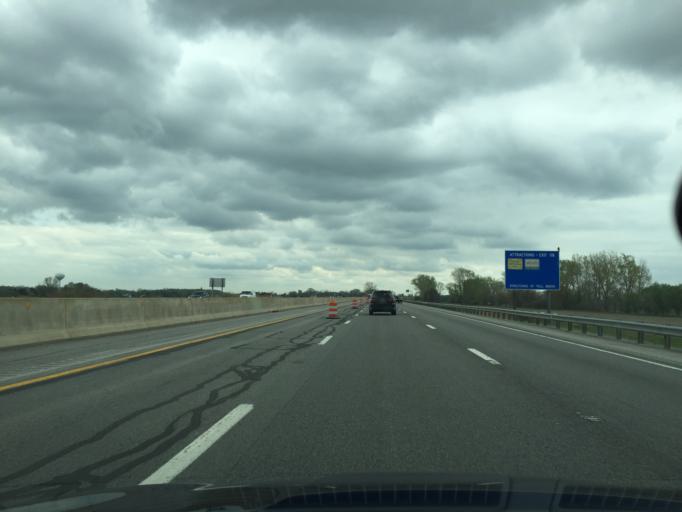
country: US
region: Ohio
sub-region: Erie County
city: Milan
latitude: 41.3277
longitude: -82.6431
